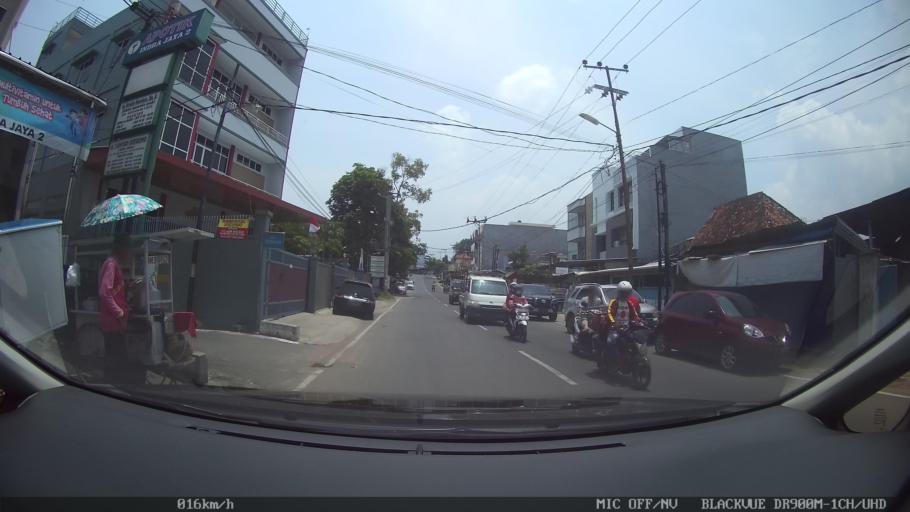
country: ID
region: Lampung
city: Bandarlampung
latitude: -5.4441
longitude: 105.2728
